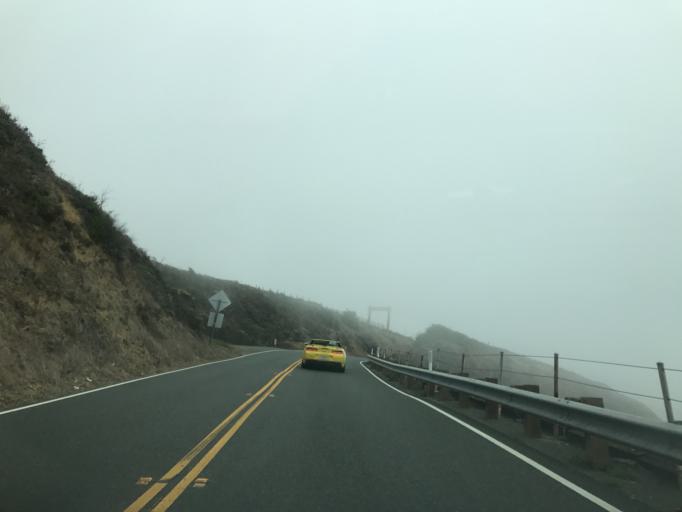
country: US
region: California
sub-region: Sonoma County
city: Monte Rio
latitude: 38.4657
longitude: -123.1531
